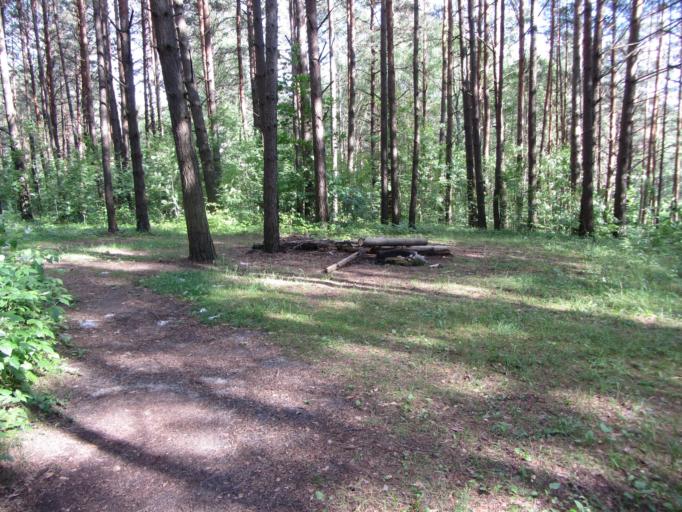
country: LT
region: Vilnius County
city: Lazdynai
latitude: 54.6793
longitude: 25.1964
